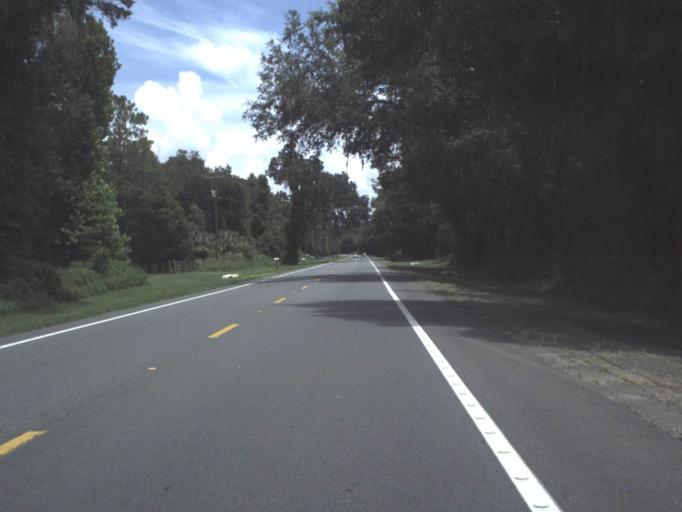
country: US
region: Florida
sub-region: Alachua County
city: Archer
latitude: 29.5479
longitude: -82.3953
